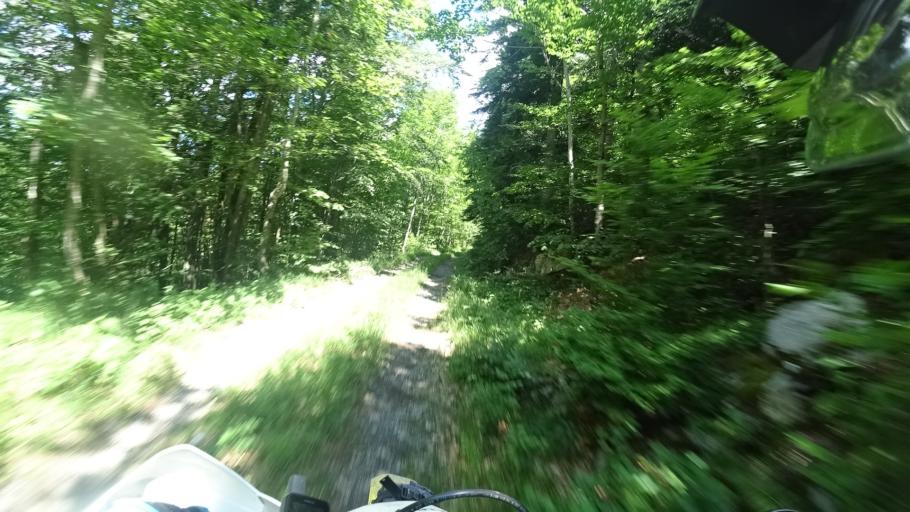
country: SI
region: Osilnica
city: Osilnica
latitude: 45.4964
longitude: 14.7169
